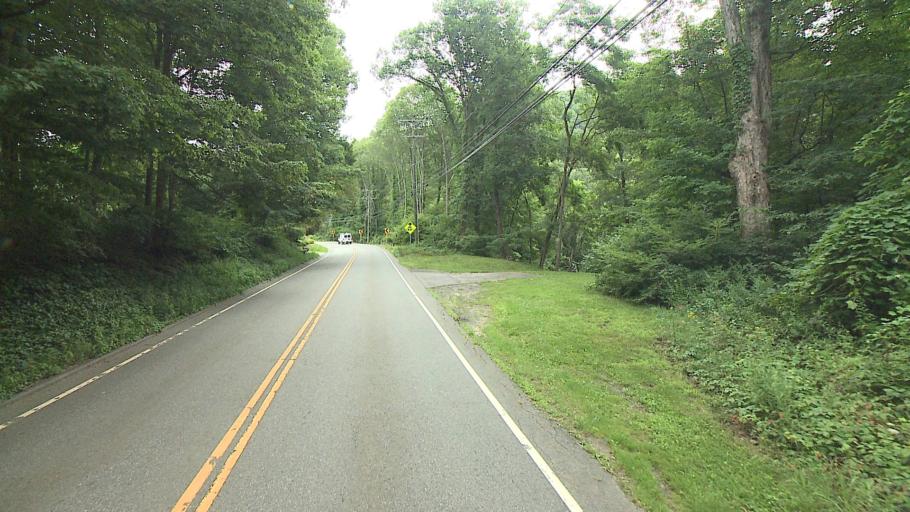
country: US
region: Connecticut
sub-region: Litchfield County
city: Kent
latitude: 41.7142
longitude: -73.4629
